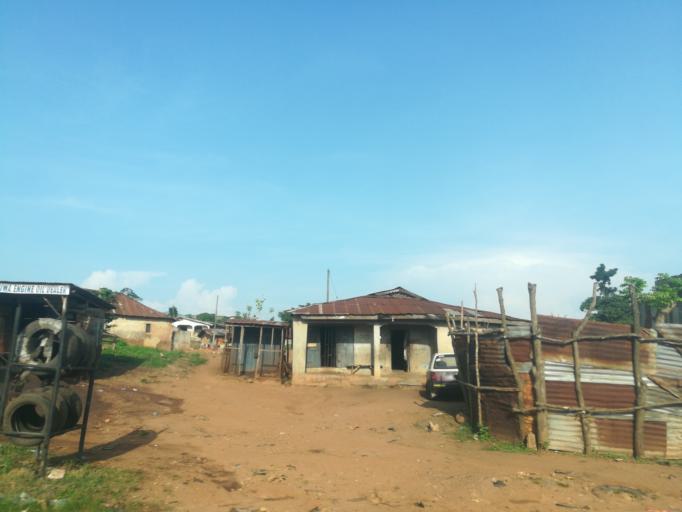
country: NG
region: Oyo
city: Moniya
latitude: 7.5203
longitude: 3.9123
